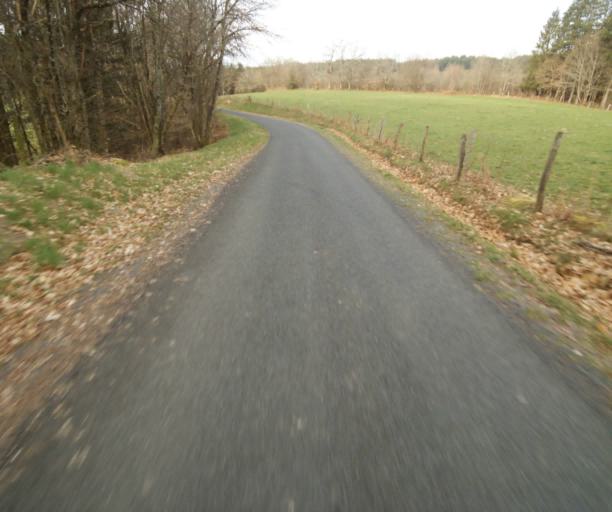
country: FR
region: Limousin
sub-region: Departement de la Correze
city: Treignac
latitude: 45.4543
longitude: 1.8103
